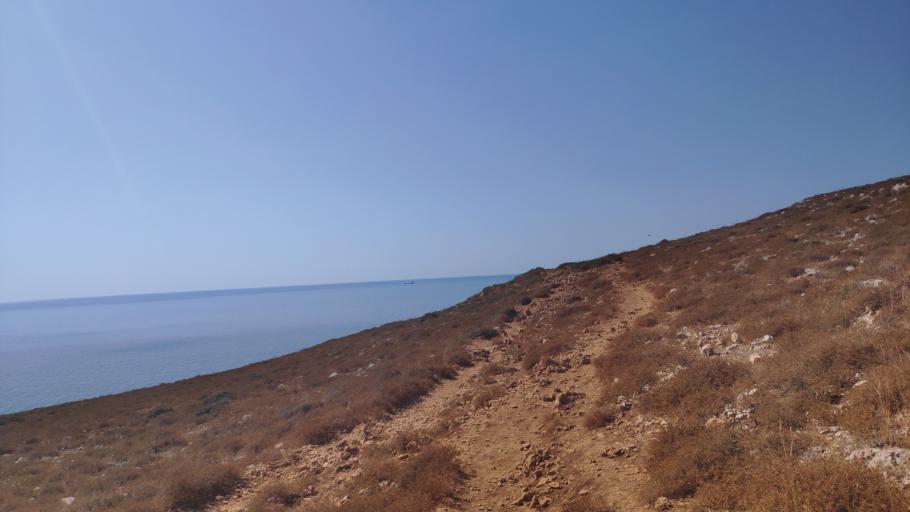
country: GR
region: Peloponnese
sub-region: Nomos Lakonias
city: Gytheio
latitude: 36.3925
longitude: 22.4837
